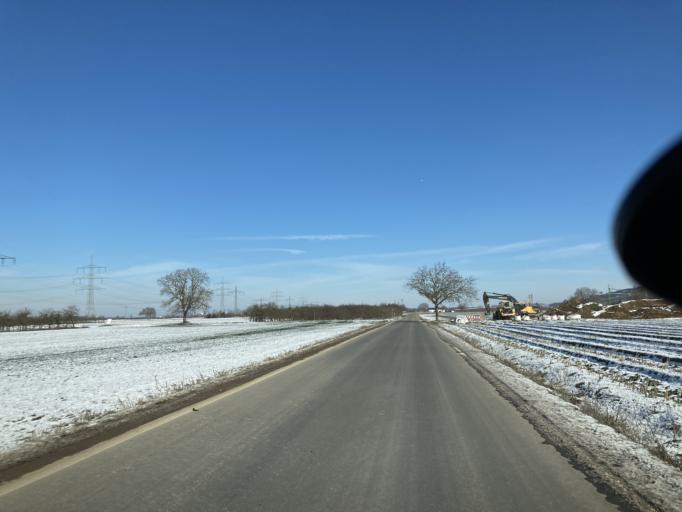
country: DE
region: Baden-Wuerttemberg
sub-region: Freiburg Region
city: Auggen
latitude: 47.7863
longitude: 7.5814
